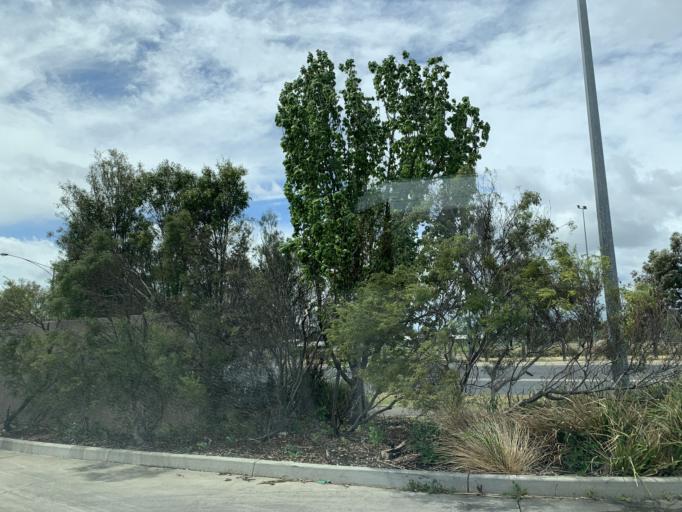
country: AU
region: Victoria
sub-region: Brimbank
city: Cairnlea
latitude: -37.7590
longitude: 144.7905
